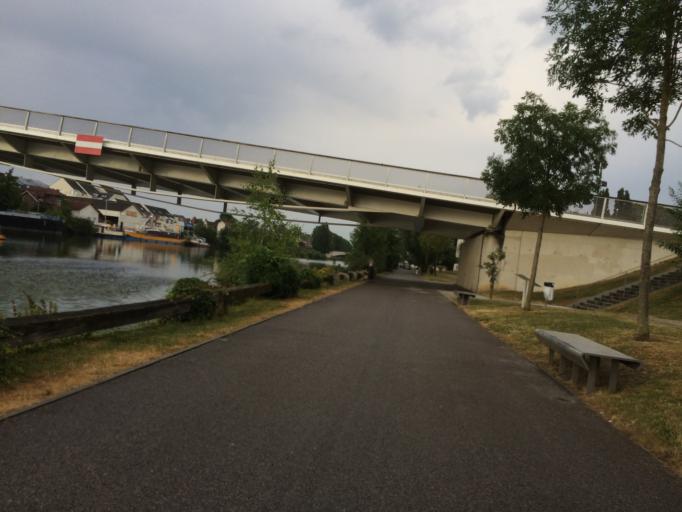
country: FR
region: Picardie
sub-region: Departement de l'Oise
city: Compiegne
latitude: 49.4167
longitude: 2.8174
